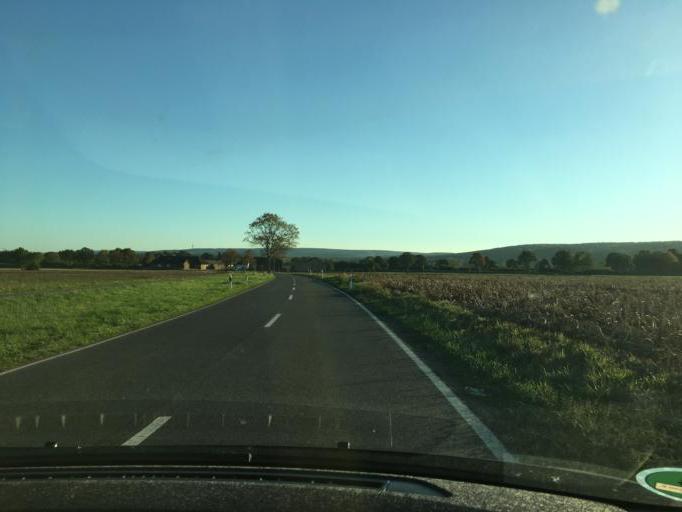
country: DE
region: North Rhine-Westphalia
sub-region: Regierungsbezirk Koln
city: Langerwehe
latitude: 50.8155
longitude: 6.3969
